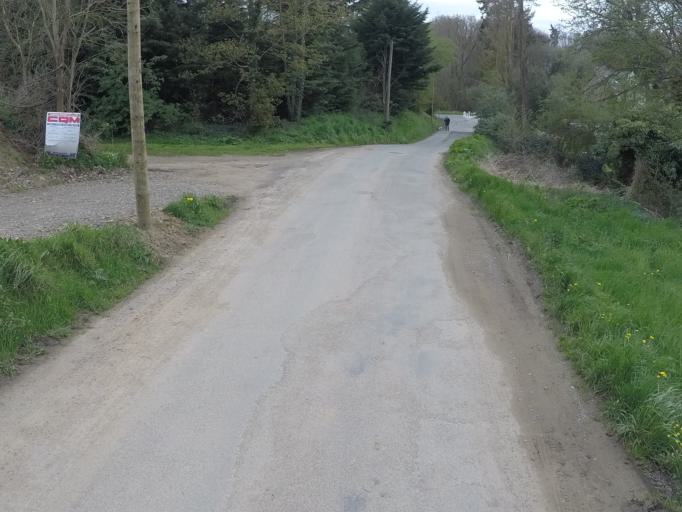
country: FR
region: Brittany
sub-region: Departement des Cotes-d'Armor
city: Plouha
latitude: 48.6712
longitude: -2.9206
